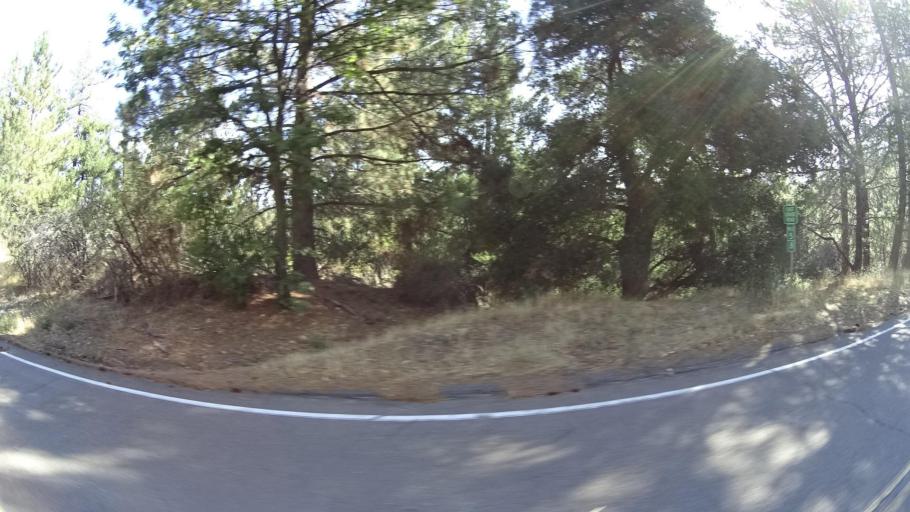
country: US
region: California
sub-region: Riverside County
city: Aguanga
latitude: 33.2861
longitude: -116.7955
